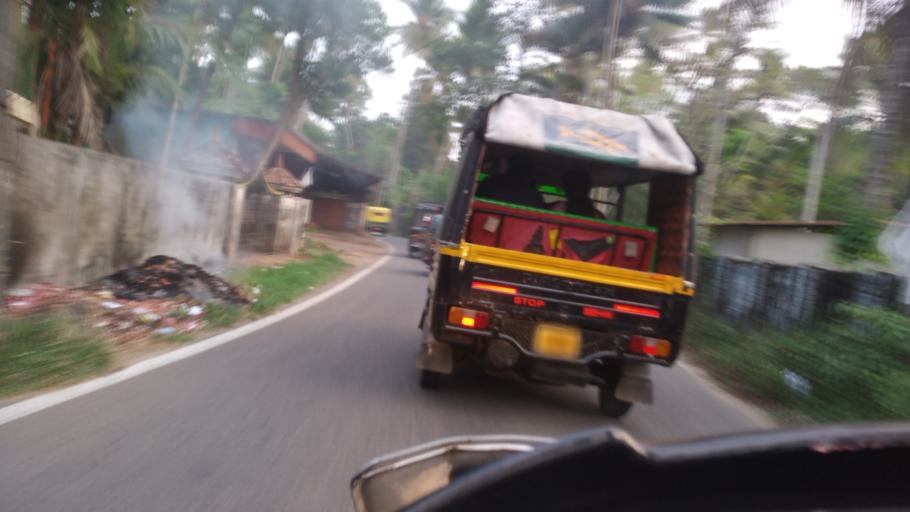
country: IN
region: Kerala
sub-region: Thrissur District
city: Kodungallur
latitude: 10.1630
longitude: 76.2087
